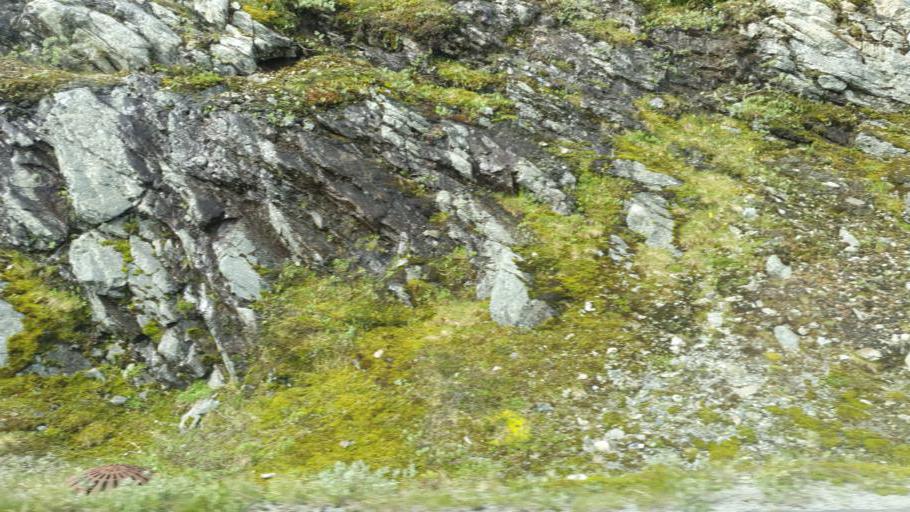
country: NO
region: Oppland
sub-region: Vestre Slidre
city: Slidre
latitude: 61.3400
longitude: 8.8146
